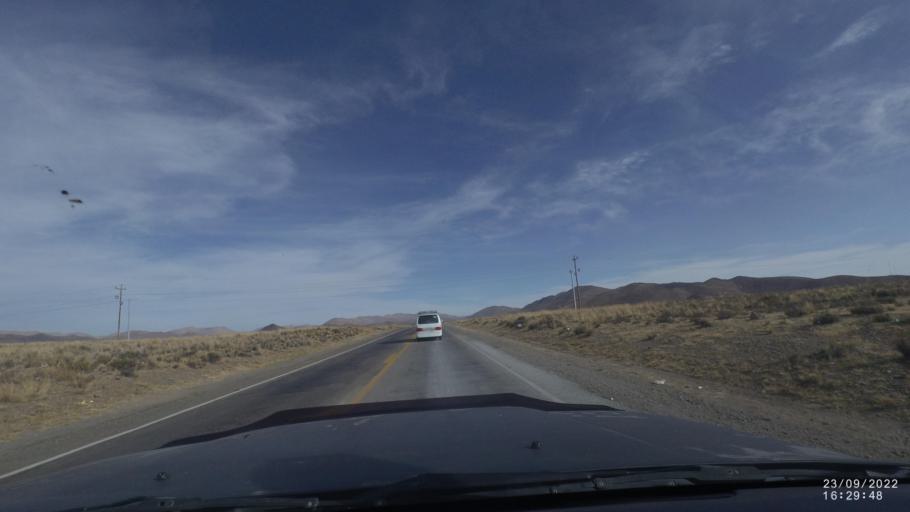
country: BO
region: Oruro
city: Machacamarca
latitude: -18.1473
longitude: -66.9904
